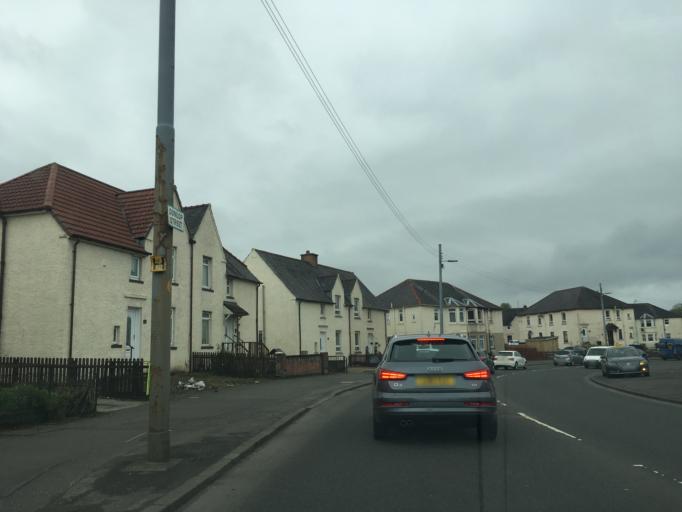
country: GB
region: Scotland
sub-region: Inverclyde
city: Greenock
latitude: 55.9405
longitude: -4.7823
